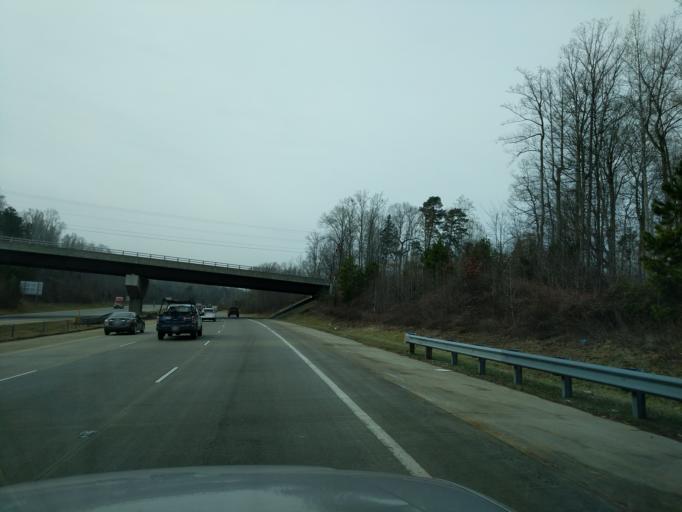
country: US
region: North Carolina
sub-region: Mecklenburg County
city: Huntersville
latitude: 35.3442
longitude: -80.8806
